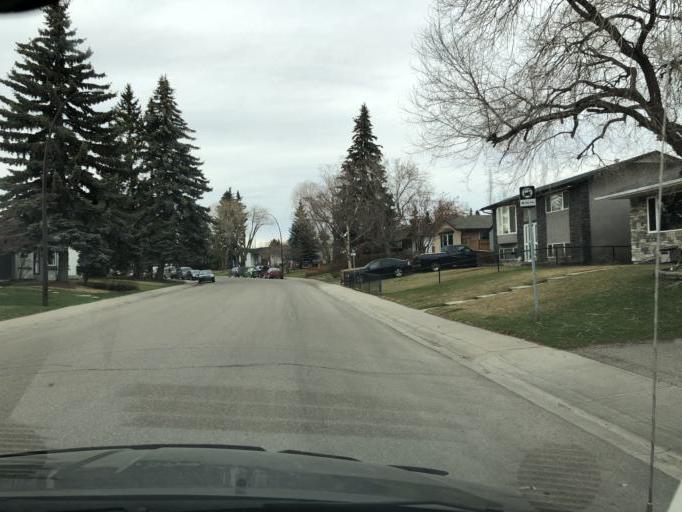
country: CA
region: Alberta
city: Calgary
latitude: 50.9443
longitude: -114.0294
